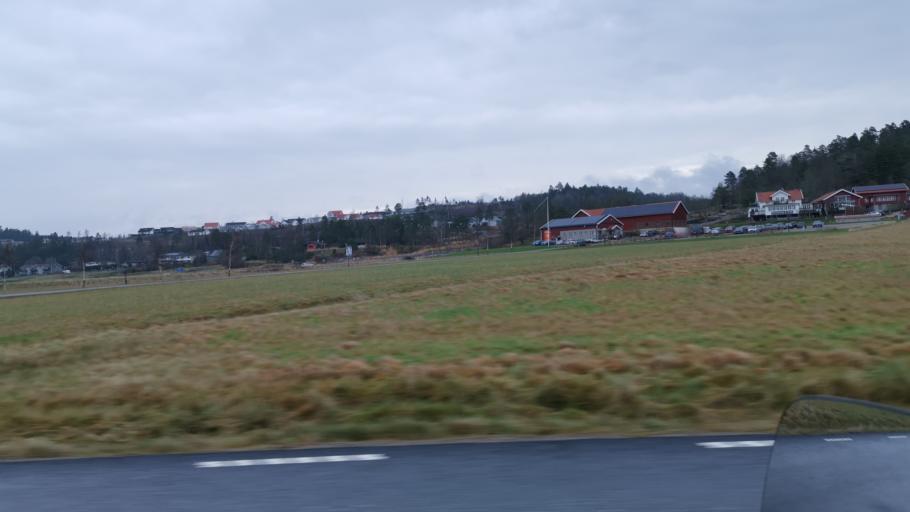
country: SE
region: Vaestra Goetaland
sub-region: Orust
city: Henan
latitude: 58.3422
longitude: 11.6989
